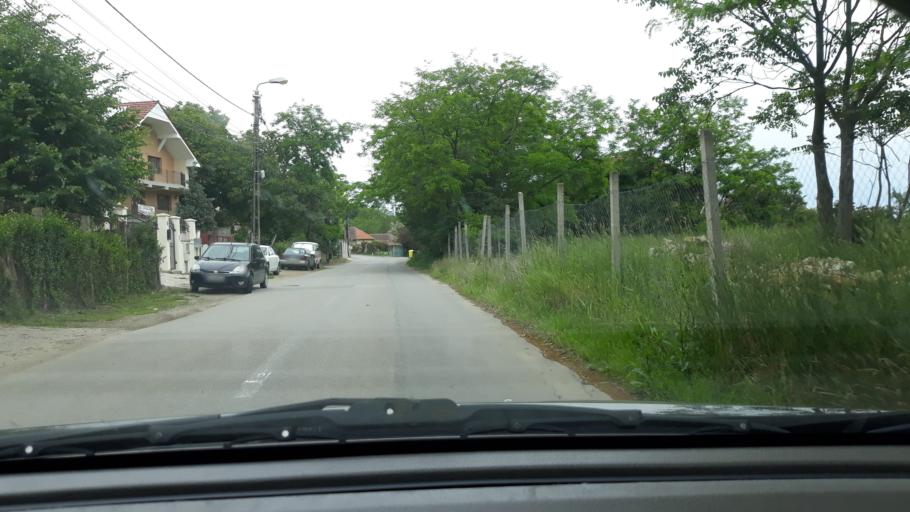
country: RO
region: Bihor
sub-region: Comuna Sanmartin
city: Sanmartin
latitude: 47.0528
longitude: 21.9783
